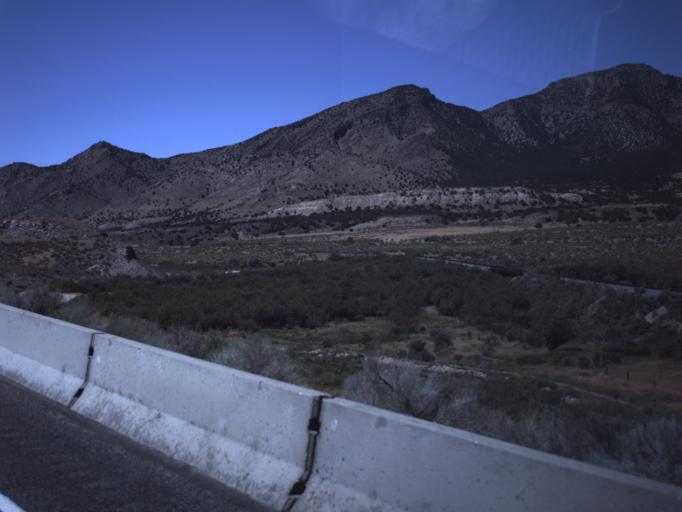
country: US
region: Utah
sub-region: Juab County
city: Nephi
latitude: 39.5568
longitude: -112.2108
